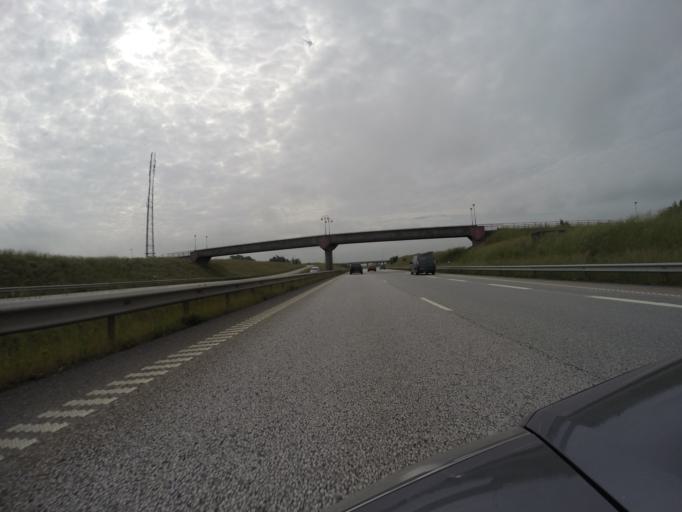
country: SE
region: Skane
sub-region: Lomma Kommun
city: Lomma
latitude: 55.7247
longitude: 13.0881
